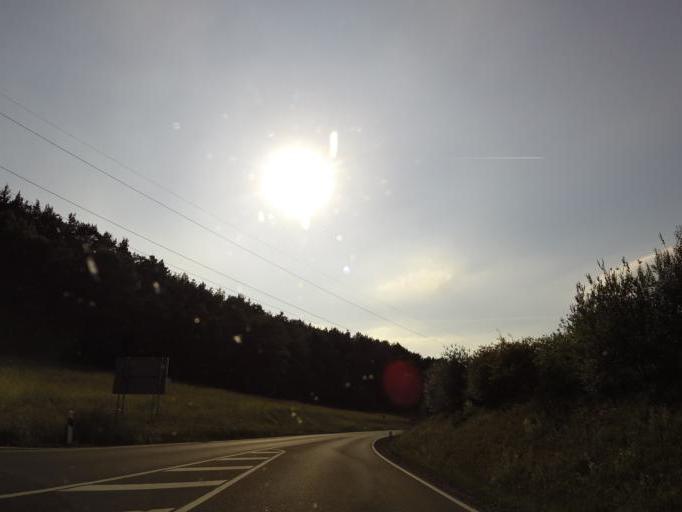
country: DE
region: Bavaria
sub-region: Regierungsbezirk Unterfranken
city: Marktheidenfeld
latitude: 49.8143
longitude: 9.6286
